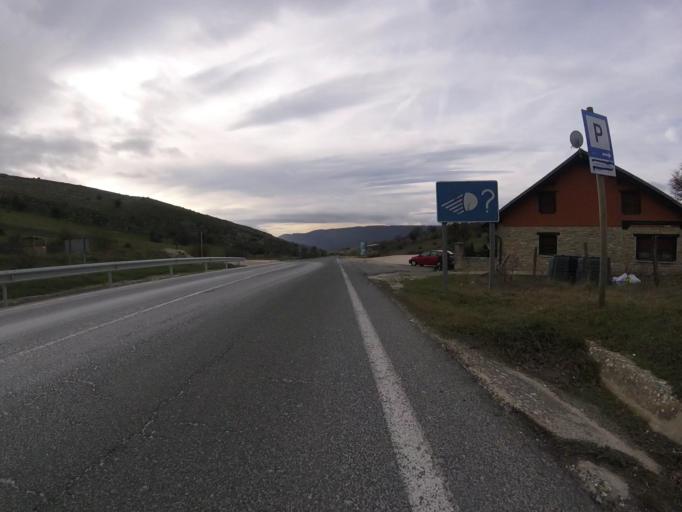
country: ES
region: Navarre
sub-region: Provincia de Navarra
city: Arbizu
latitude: 42.8597
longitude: -2.0114
